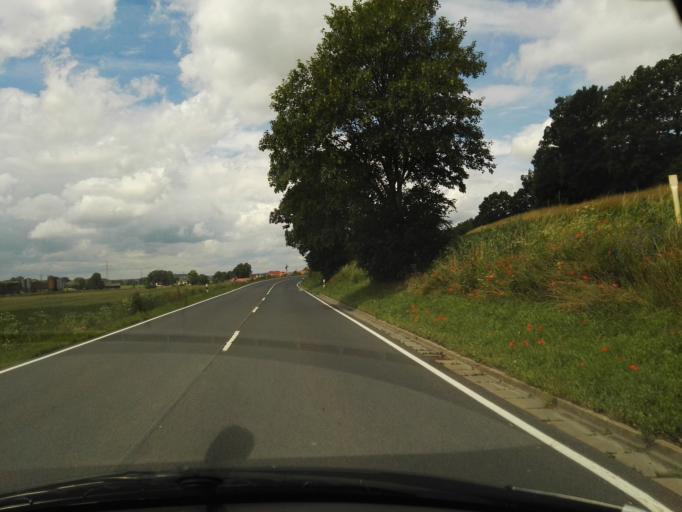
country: DE
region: Bavaria
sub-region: Upper Franconia
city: Redwitz an der Rodach
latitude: 50.1482
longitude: 11.2229
